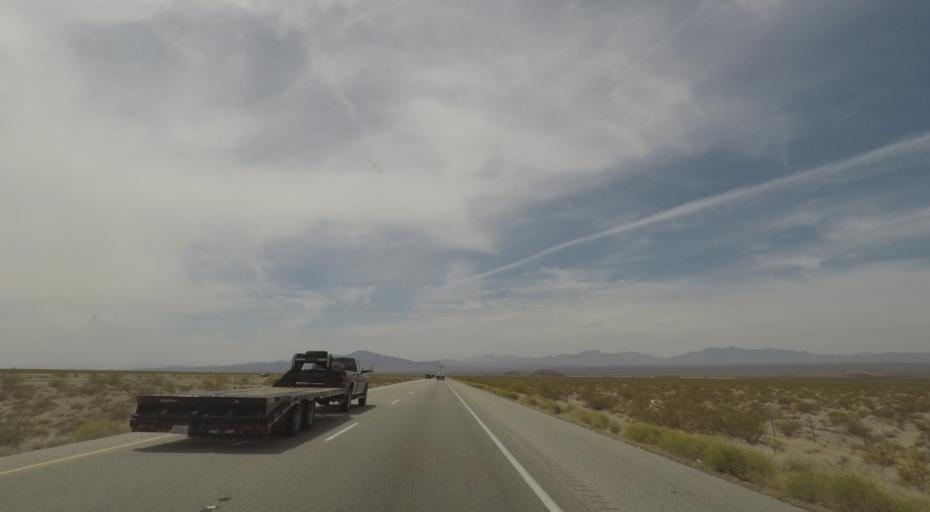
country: US
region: California
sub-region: San Bernardino County
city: Needles
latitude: 34.8202
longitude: -115.1281
